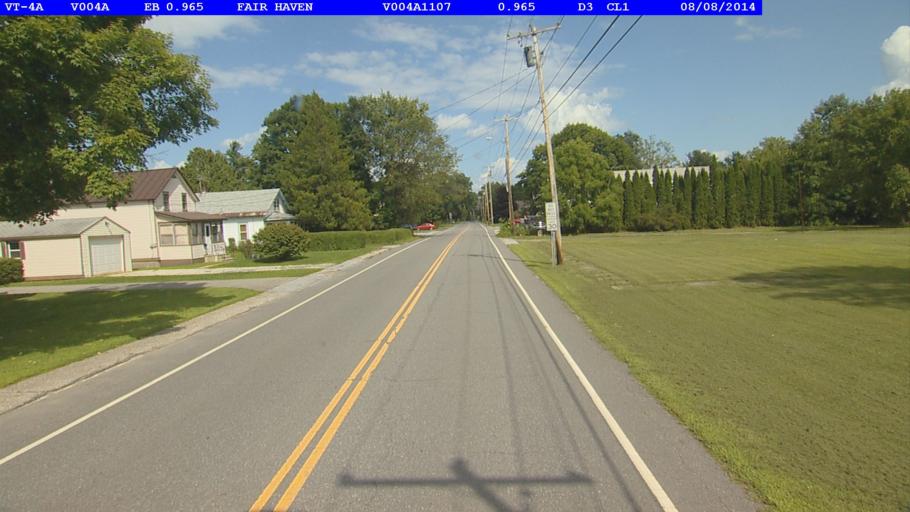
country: US
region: Vermont
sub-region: Rutland County
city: Fair Haven
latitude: 43.5870
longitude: -73.2747
